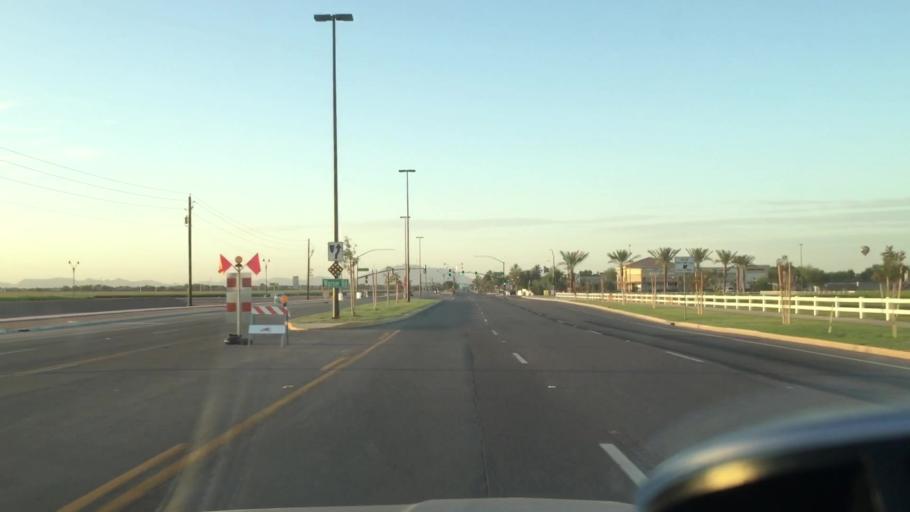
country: US
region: Arizona
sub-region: Maricopa County
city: Gilbert
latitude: 33.3379
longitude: -111.7214
